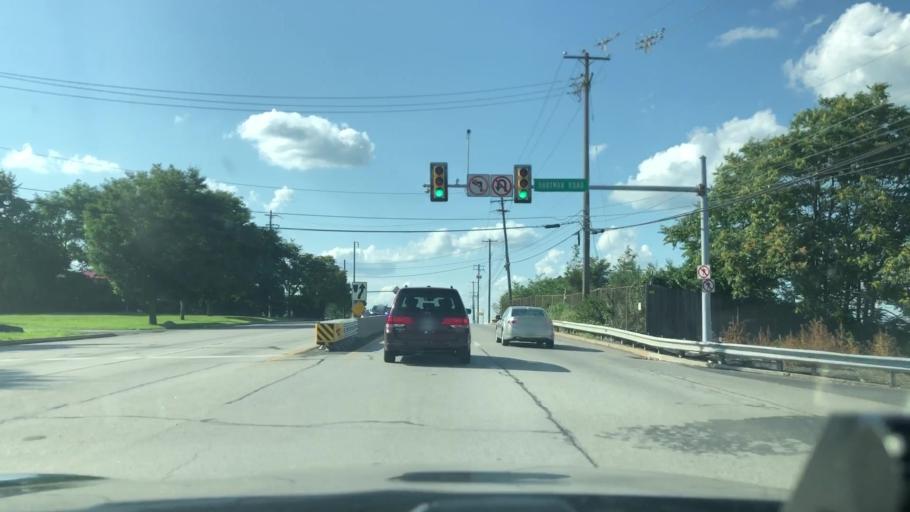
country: US
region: Pennsylvania
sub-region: Montgomery County
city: Spring House
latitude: 40.2172
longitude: -75.2289
